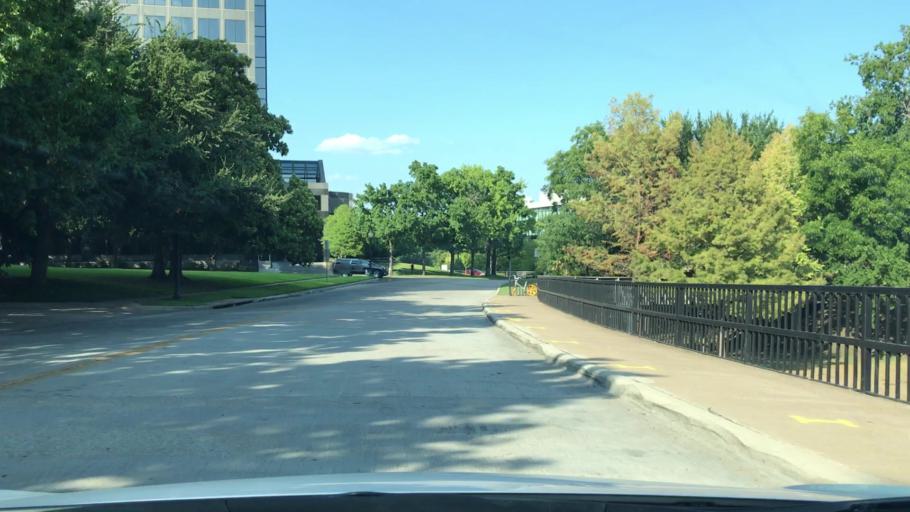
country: US
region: Texas
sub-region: Dallas County
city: Dallas
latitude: 32.8033
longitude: -96.8068
